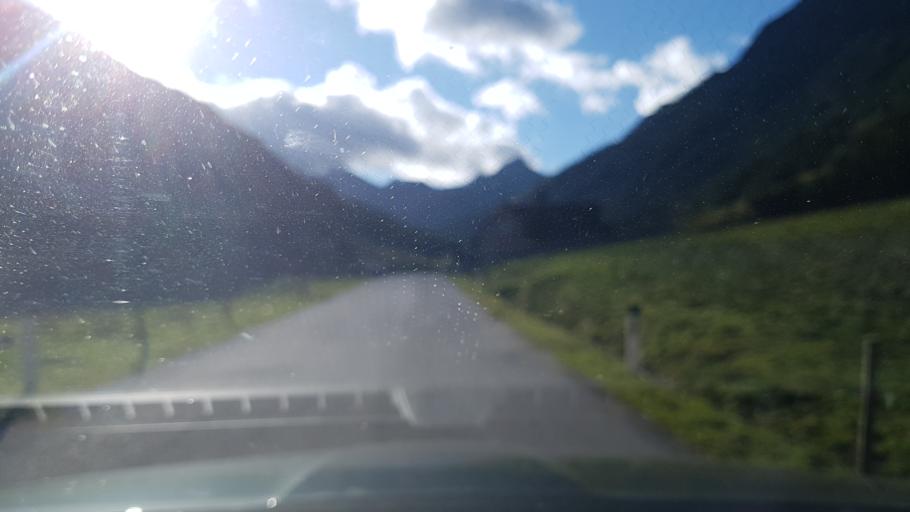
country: AT
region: Styria
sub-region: Politischer Bezirk Liezen
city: Sankt Nikolai im Solktal
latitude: 47.3114
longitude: 14.0586
